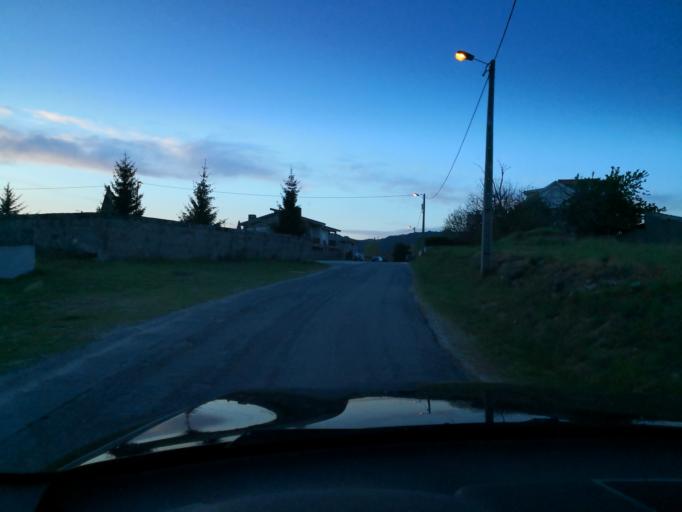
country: PT
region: Vila Real
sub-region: Vila Real
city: Vila Real
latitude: 41.3680
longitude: -7.6556
